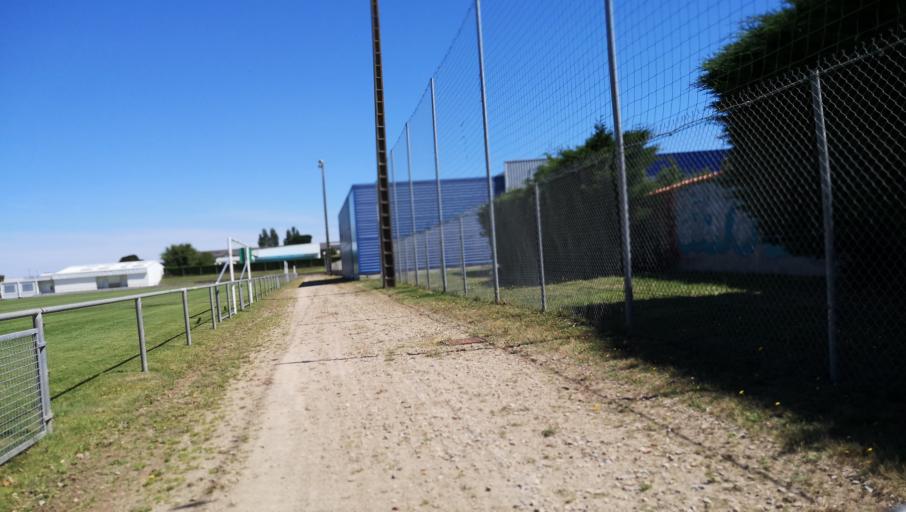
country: FR
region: Pays de la Loire
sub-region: Departement de la Vendee
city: Les Sables-d'Olonne
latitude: 46.5092
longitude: -1.7735
